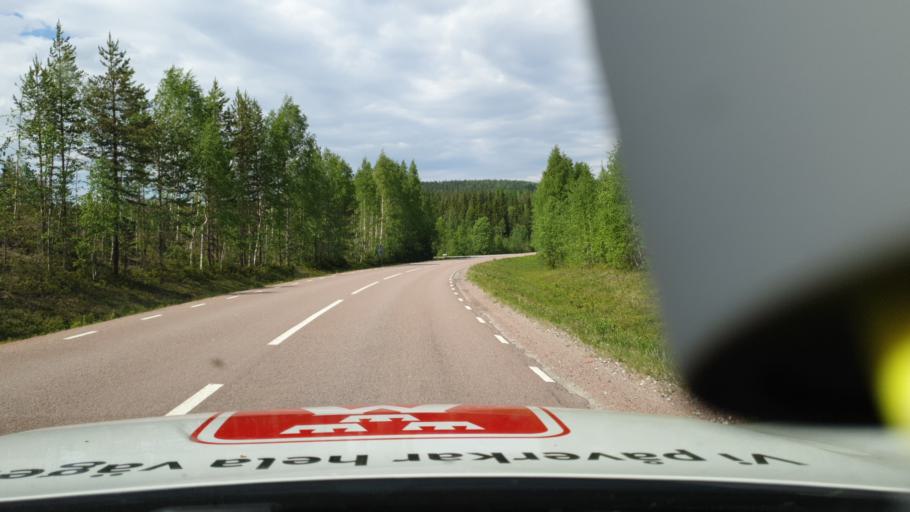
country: SE
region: Jaemtland
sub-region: Braecke Kommun
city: Braecke
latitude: 62.9590
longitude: 15.7479
